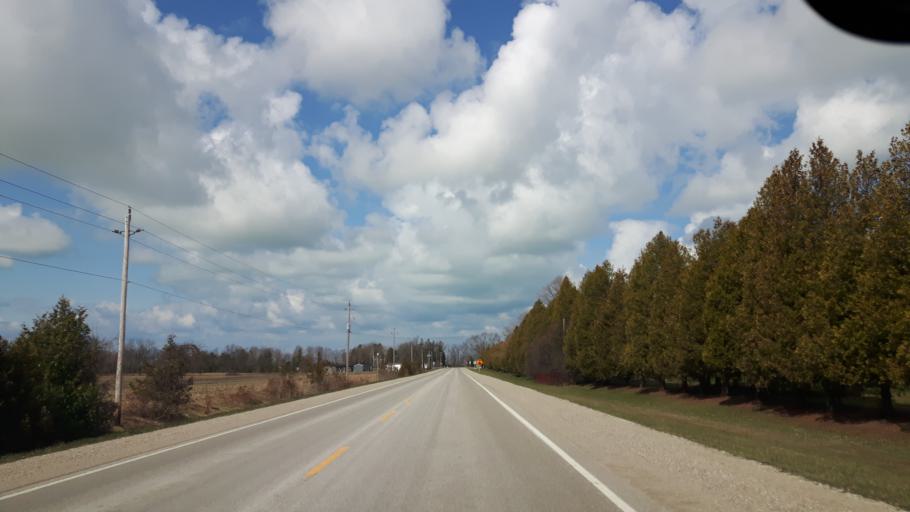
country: CA
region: Ontario
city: Bluewater
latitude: 43.5870
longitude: -81.6996
